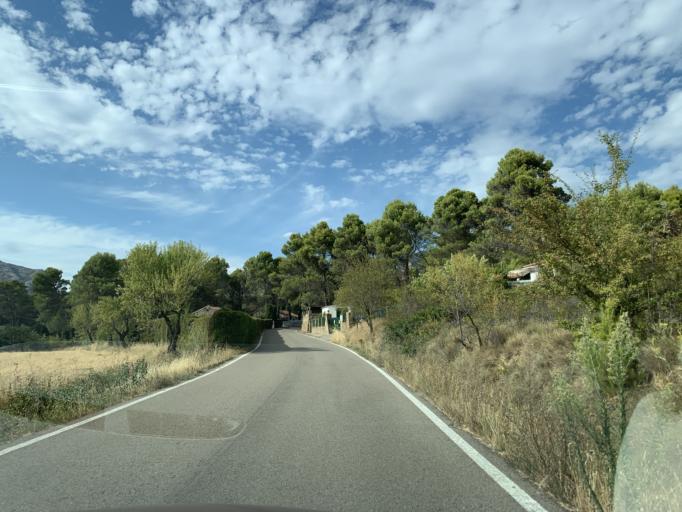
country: ES
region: Aragon
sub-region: Provincia de Zaragoza
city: Santa Eulalia de Gallego
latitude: 42.3222
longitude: -0.7242
